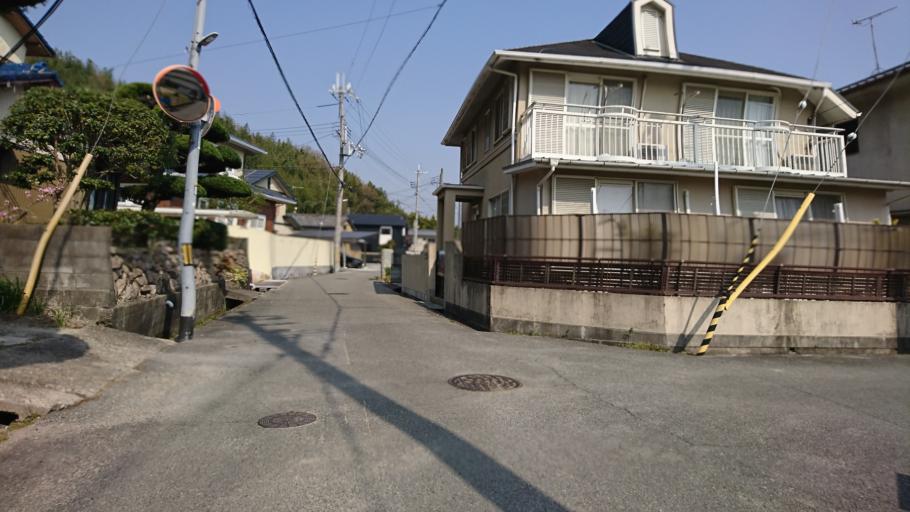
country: JP
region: Hyogo
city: Shirahamacho-usazakiminami
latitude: 34.7840
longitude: 134.7676
